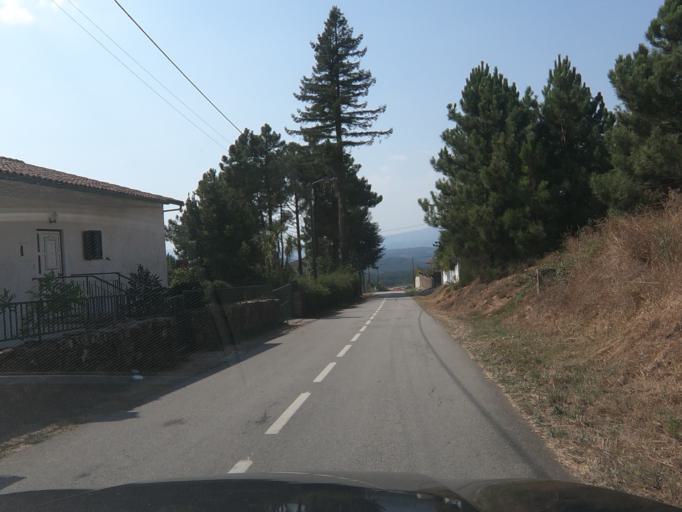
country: PT
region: Vila Real
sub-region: Sabrosa
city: Sabrosa
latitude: 41.2724
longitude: -7.6182
